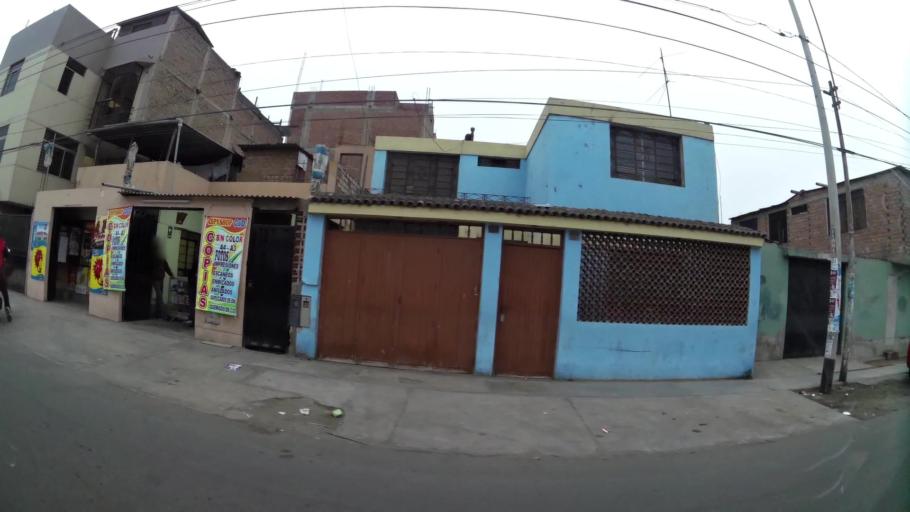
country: PE
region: Lima
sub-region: Lima
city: Surco
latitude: -12.1660
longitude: -76.9728
